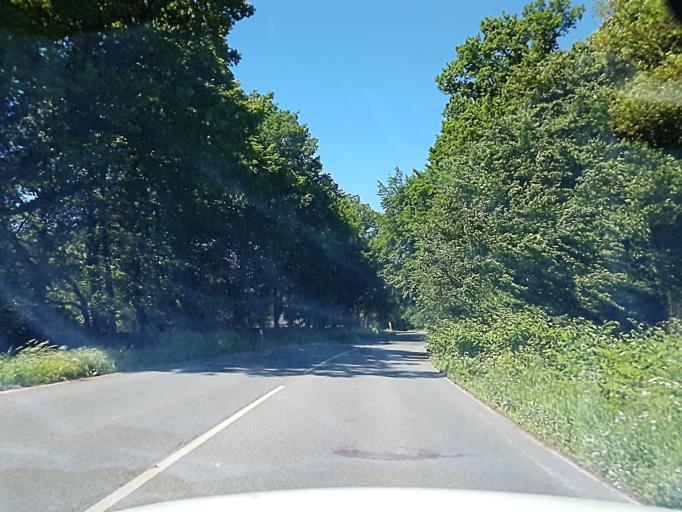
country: DE
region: North Rhine-Westphalia
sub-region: Regierungsbezirk Dusseldorf
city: Ratingen
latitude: 51.3370
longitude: 6.8078
